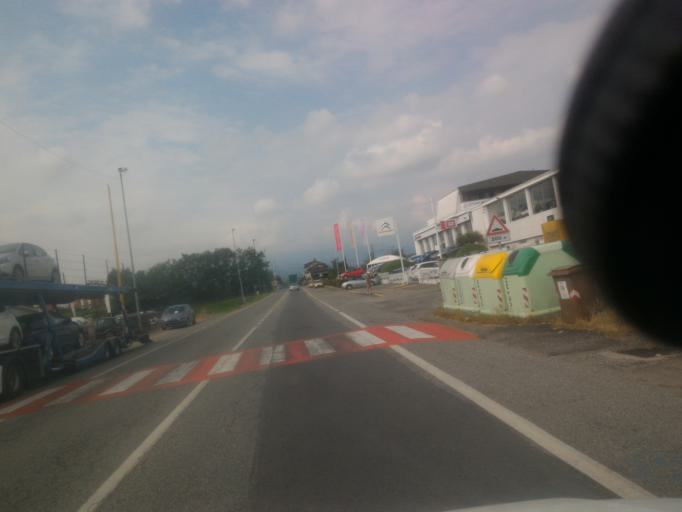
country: IT
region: Piedmont
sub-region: Provincia di Torino
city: Osasco
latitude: 44.8528
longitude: 7.3207
